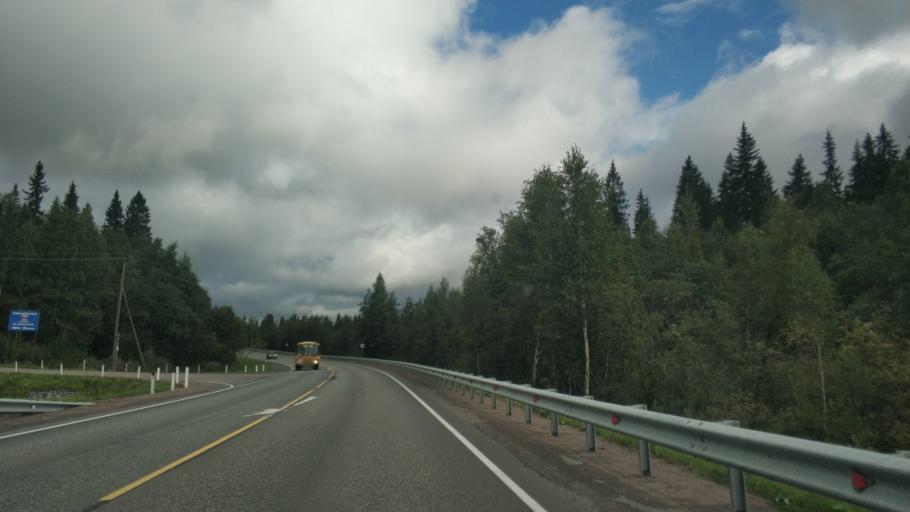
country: RU
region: Republic of Karelia
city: Khelyulya
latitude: 61.7822
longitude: 30.6572
